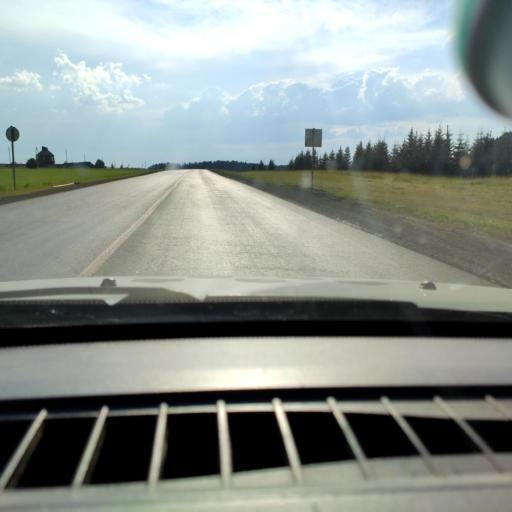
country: RU
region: Udmurtiya
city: Debesy
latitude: 57.6943
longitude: 53.9885
